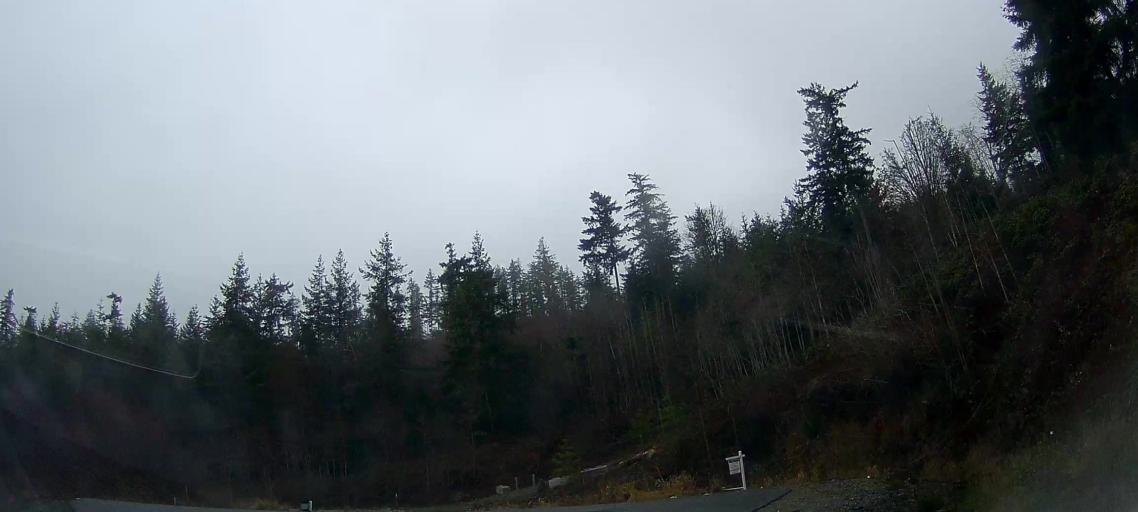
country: US
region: Washington
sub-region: Skagit County
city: Mount Vernon
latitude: 48.3692
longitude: -122.3005
